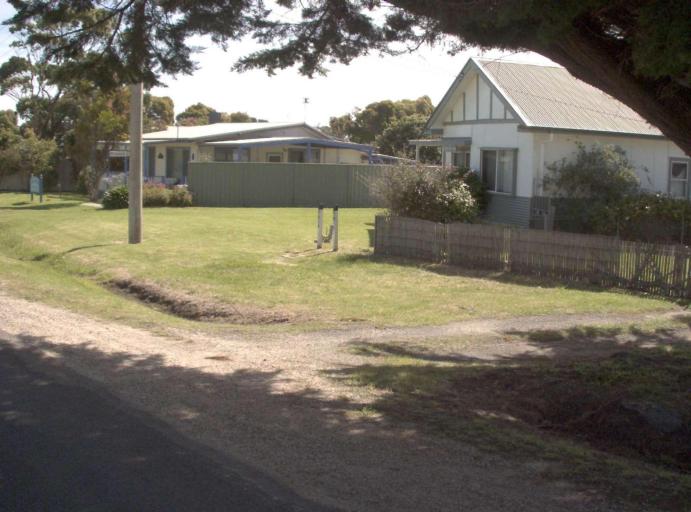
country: AU
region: Victoria
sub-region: Wellington
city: Sale
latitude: -38.3728
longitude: 147.1882
